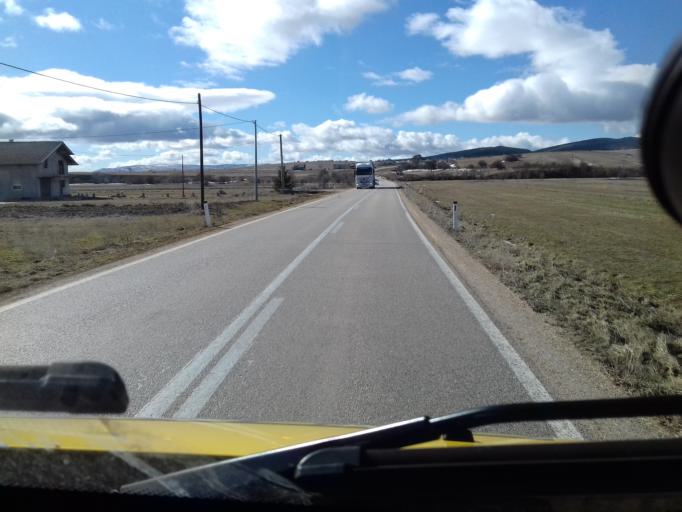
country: BA
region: Federation of Bosnia and Herzegovina
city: Tomislavgrad
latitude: 43.7593
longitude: 17.2344
